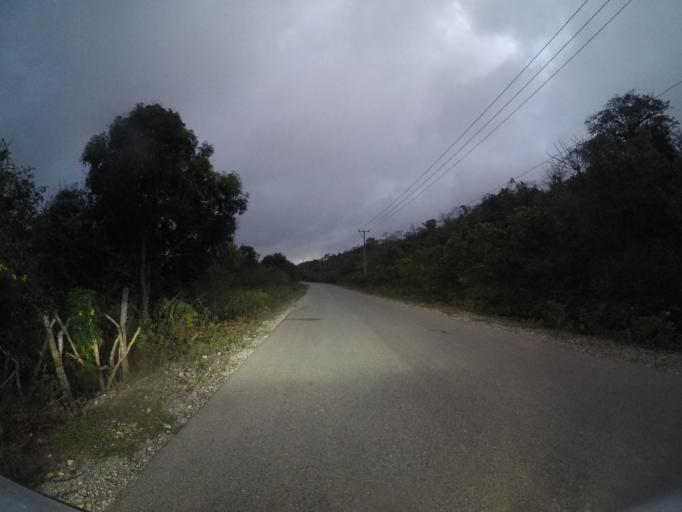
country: TL
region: Lautem
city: Lospalos
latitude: -8.4067
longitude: 127.0004
